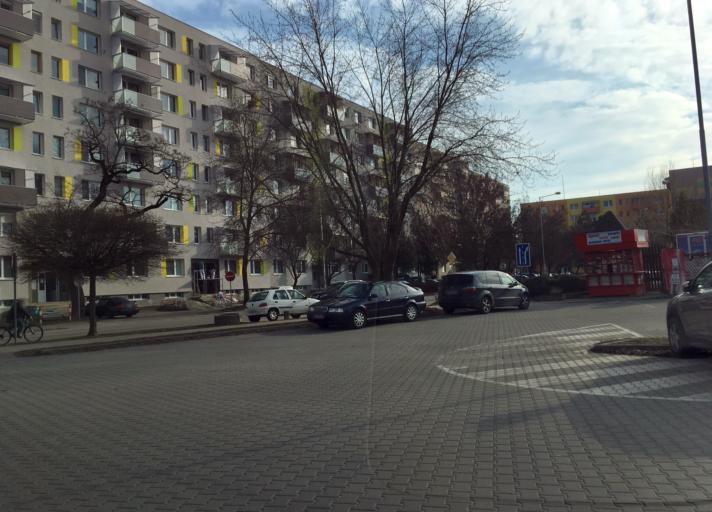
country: SK
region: Nitriansky
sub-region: Okres Nove Zamky
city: Nove Zamky
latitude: 47.9830
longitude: 18.1669
